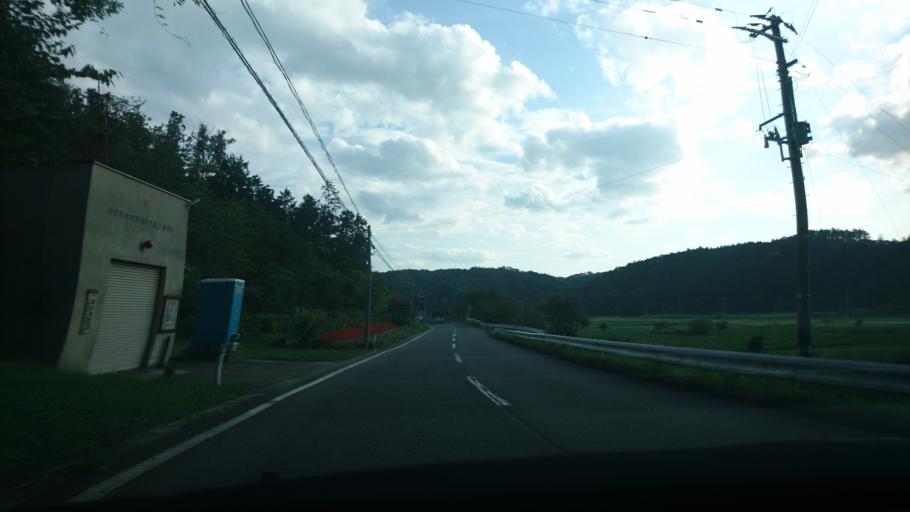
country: JP
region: Iwate
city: Ichinoseki
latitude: 39.0219
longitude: 141.2912
